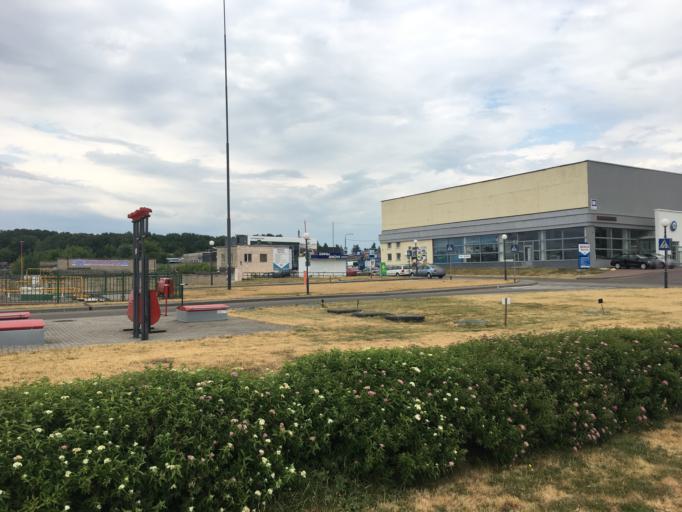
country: BY
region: Grodnenskaya
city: Hrodna
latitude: 53.6733
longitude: 23.8711
